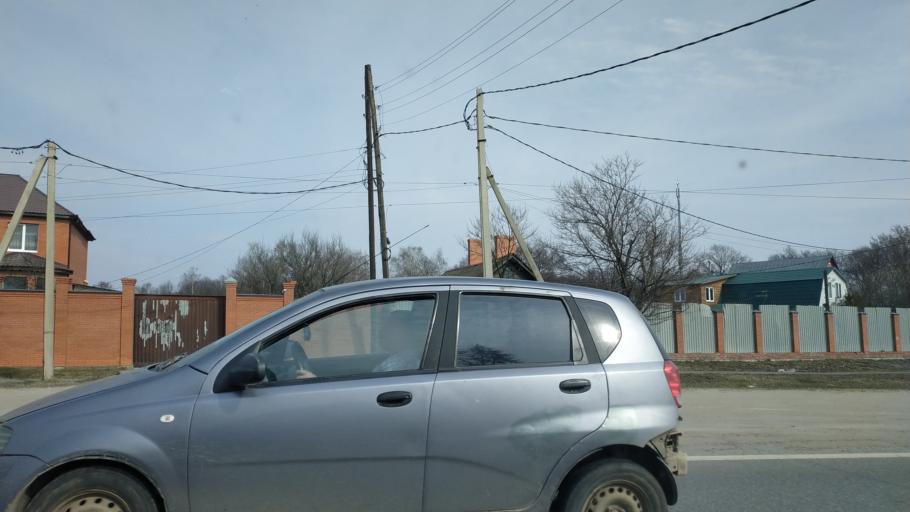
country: RU
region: Moskovskaya
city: Bronnitsy
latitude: 55.3958
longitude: 38.3215
